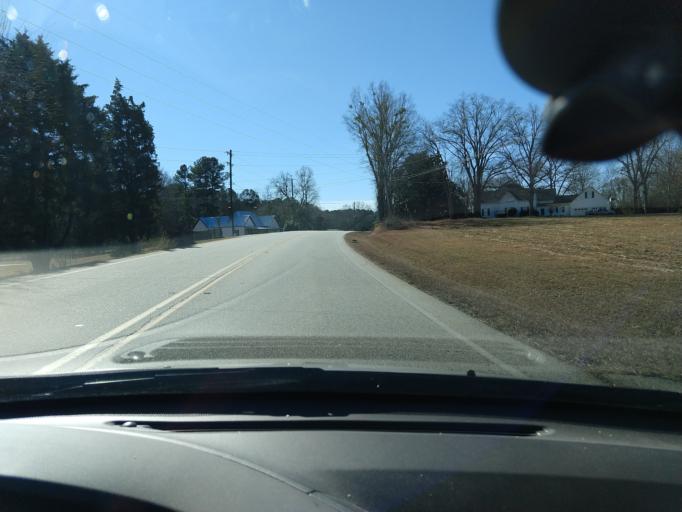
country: US
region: Georgia
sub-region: Walton County
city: Social Circle
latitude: 33.5131
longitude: -83.7328
